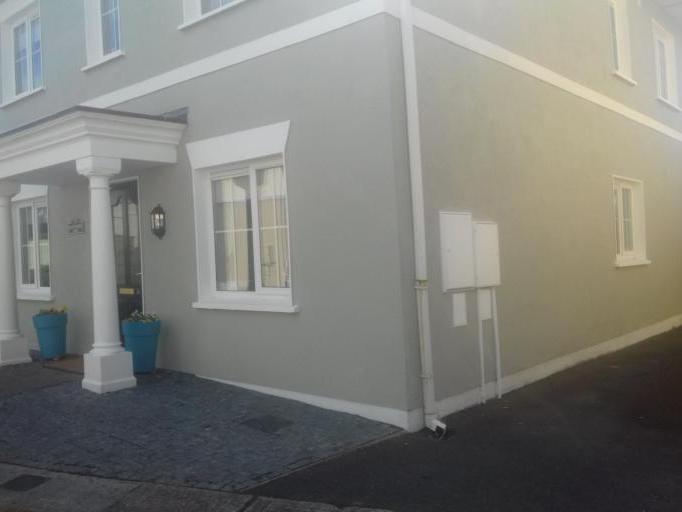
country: IE
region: Leinster
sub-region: Laois
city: Portlaoise
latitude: 53.0432
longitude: -7.2987
